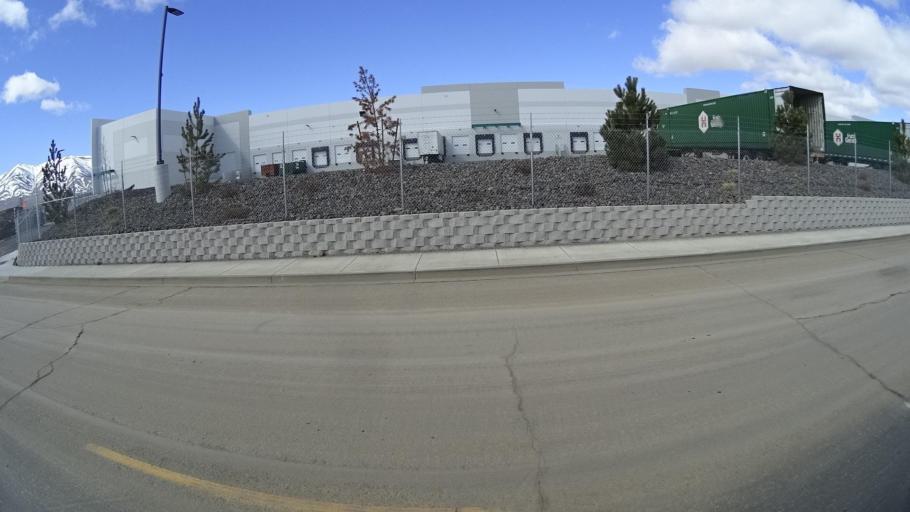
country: US
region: Nevada
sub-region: Washoe County
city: Lemmon Valley
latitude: 39.6541
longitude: -119.8695
